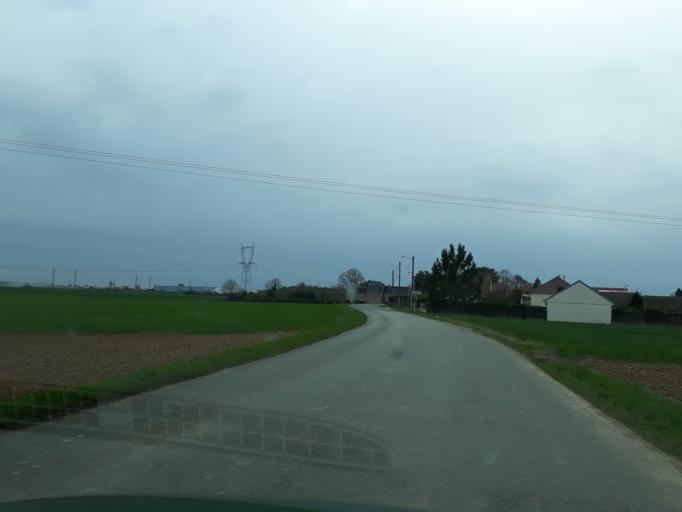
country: FR
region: Centre
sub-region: Departement du Loir-et-Cher
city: Villebarou
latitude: 47.6432
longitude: 1.2999
